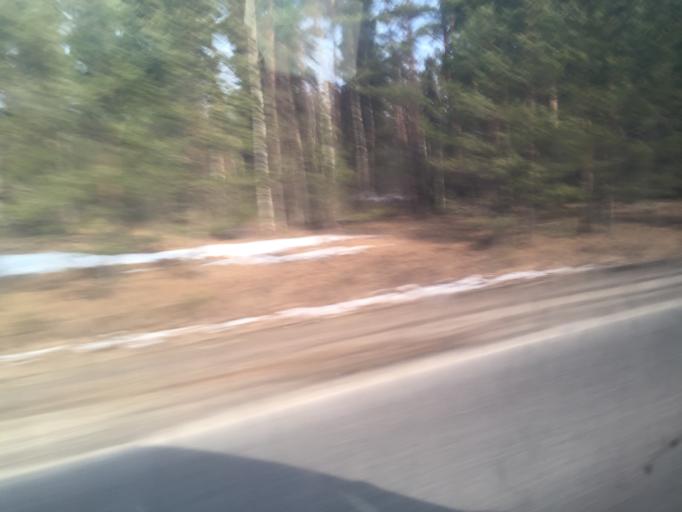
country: RU
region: Ivanovo
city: Lezhnevo
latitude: 56.8299
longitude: 40.8952
